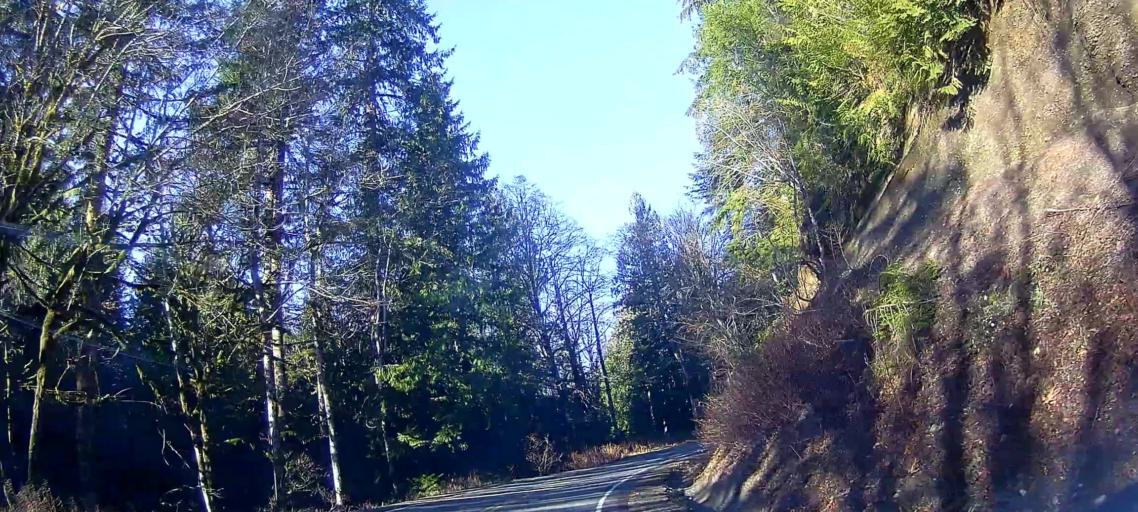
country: US
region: Washington
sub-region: Snohomish County
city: Darrington
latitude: 48.5503
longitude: -121.7671
